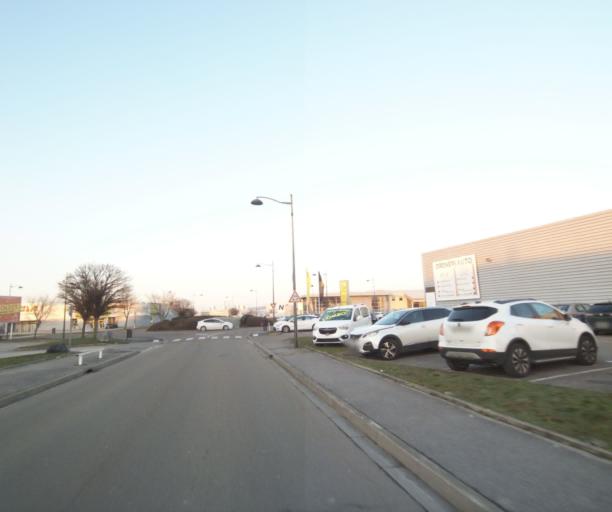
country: FR
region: Champagne-Ardenne
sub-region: Departement de la Haute-Marne
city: Saint-Dizier
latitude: 48.6240
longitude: 4.9697
